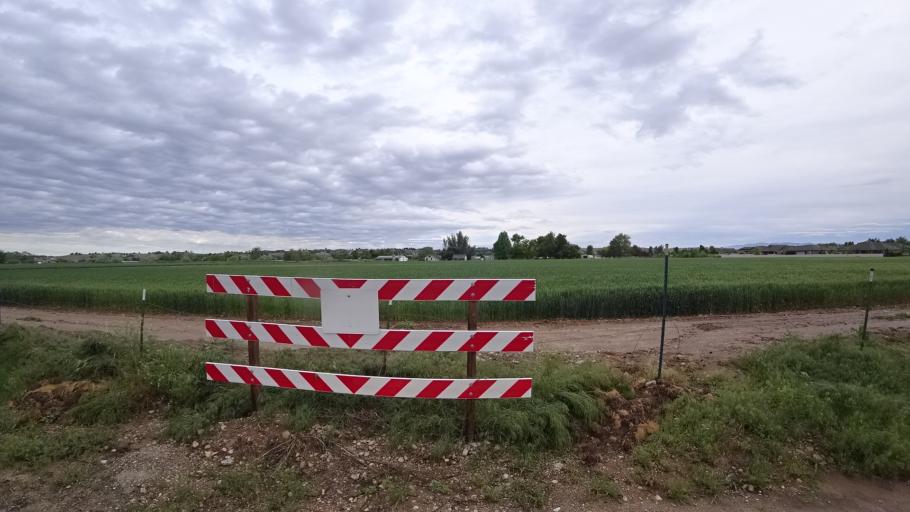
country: US
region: Idaho
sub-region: Ada County
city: Star
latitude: 43.7038
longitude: -116.5051
